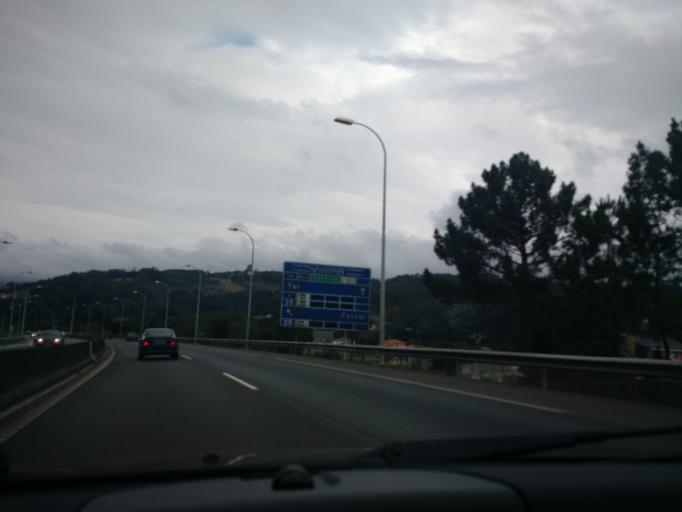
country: ES
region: Galicia
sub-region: Provincia da Coruna
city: Culleredo
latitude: 43.3199
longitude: -8.3925
